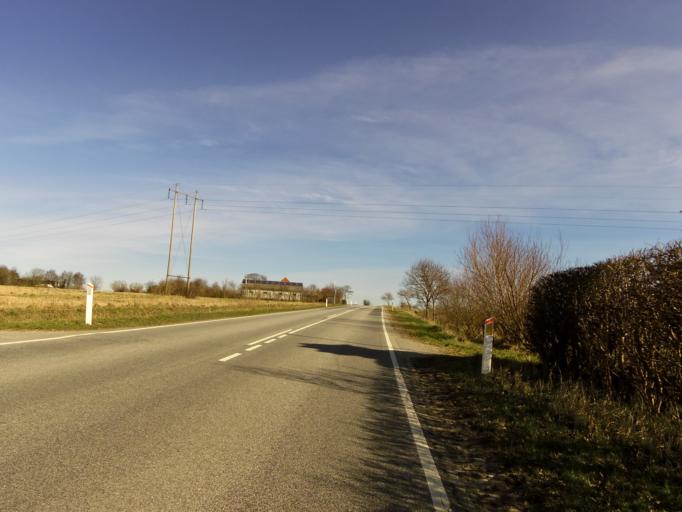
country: DK
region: South Denmark
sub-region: Vejen Kommune
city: Rodding
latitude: 55.3649
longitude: 9.0913
